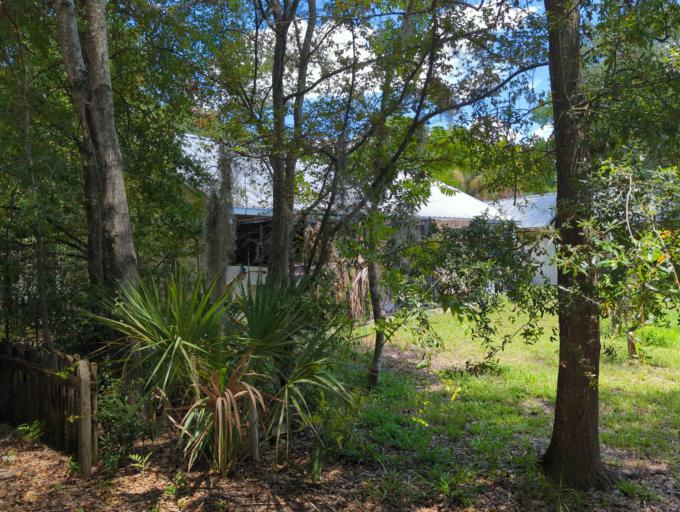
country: US
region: Florida
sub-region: Duval County
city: Jacksonville
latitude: 30.4020
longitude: -81.6436
